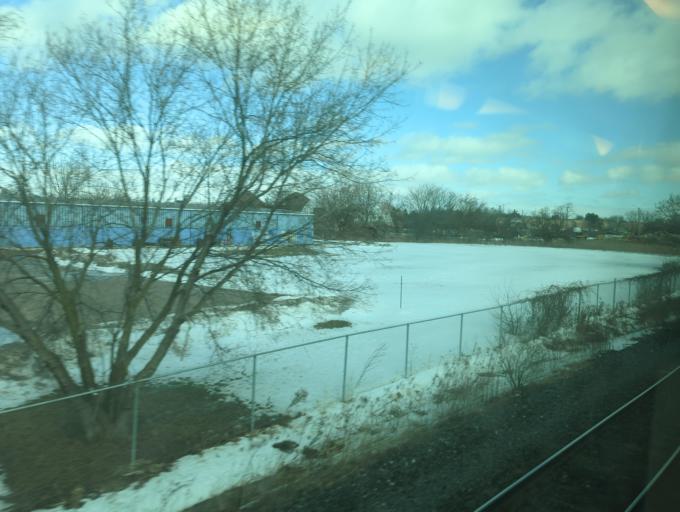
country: CA
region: Ontario
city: Burlington
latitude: 43.3543
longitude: -79.7880
